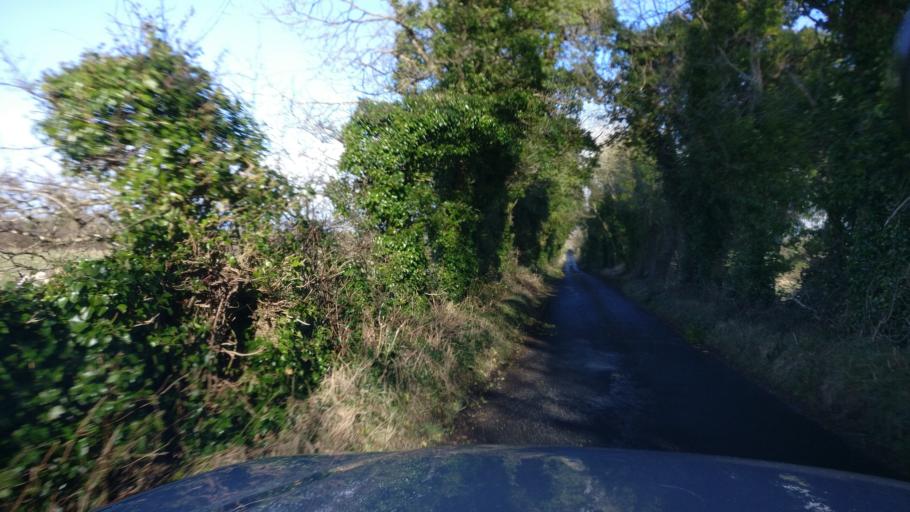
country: IE
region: Connaught
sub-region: County Galway
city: Loughrea
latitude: 53.2167
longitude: -8.6671
